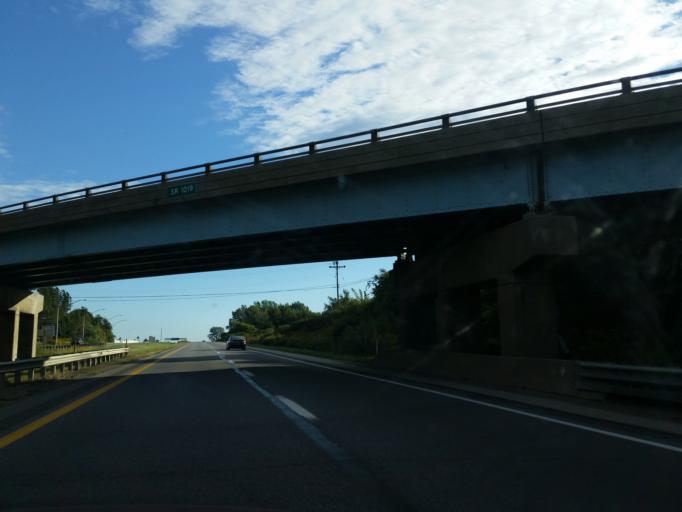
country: US
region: Pennsylvania
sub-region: Erie County
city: North East
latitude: 42.2437
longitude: -79.7718
